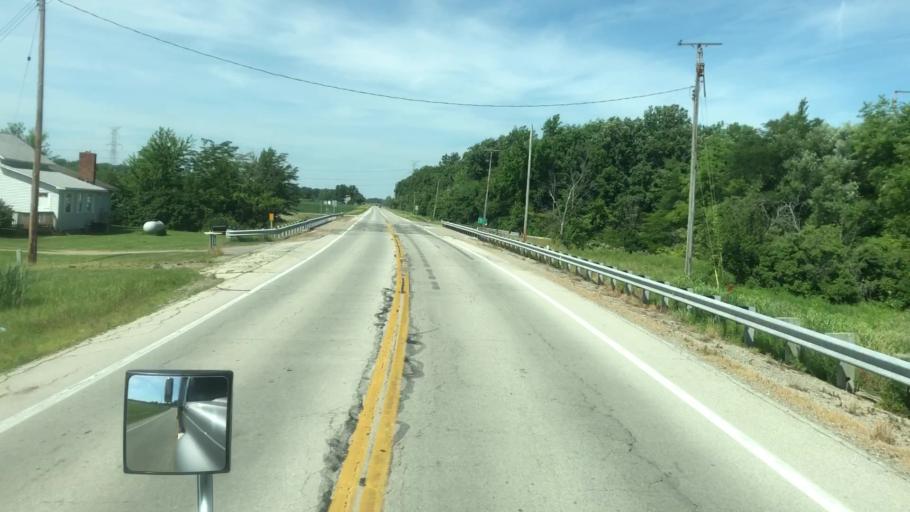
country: US
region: Ohio
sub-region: Sandusky County
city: Clyde
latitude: 41.4081
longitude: -82.9812
